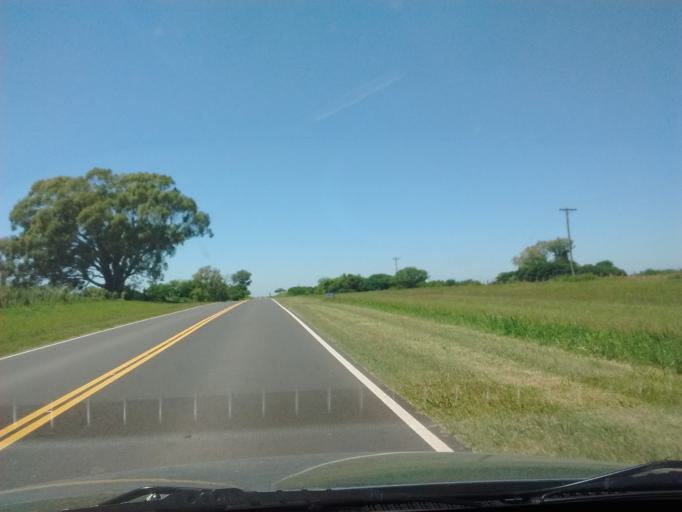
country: AR
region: Entre Rios
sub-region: Departamento de Victoria
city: Victoria
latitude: -32.8287
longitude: -59.8742
